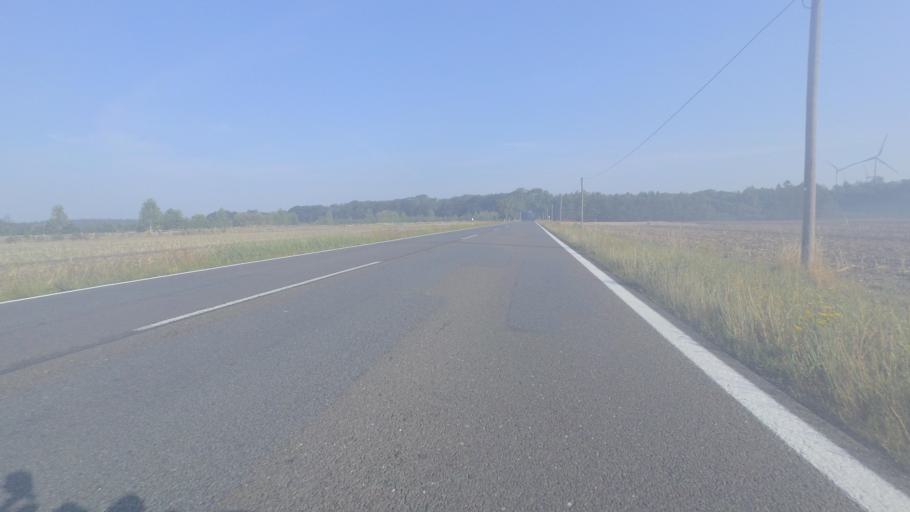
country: DE
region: Mecklenburg-Vorpommern
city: Grimmen
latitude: 54.0332
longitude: 13.1294
